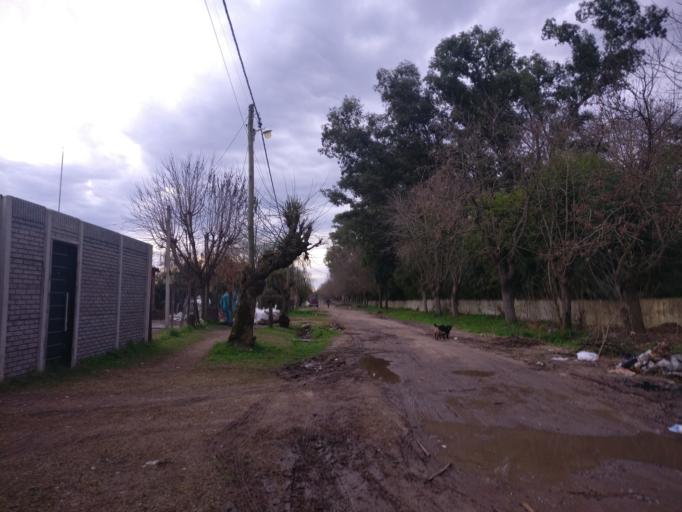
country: AR
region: Buenos Aires
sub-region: Partido de Ezeiza
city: Ezeiza
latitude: -34.9389
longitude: -58.6136
